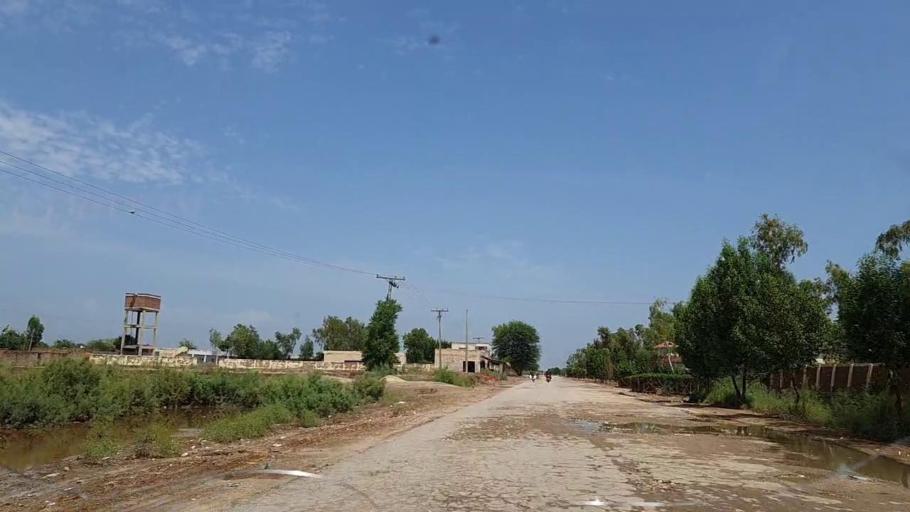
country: PK
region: Sindh
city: Naushahro Firoz
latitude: 26.8304
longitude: 68.1405
